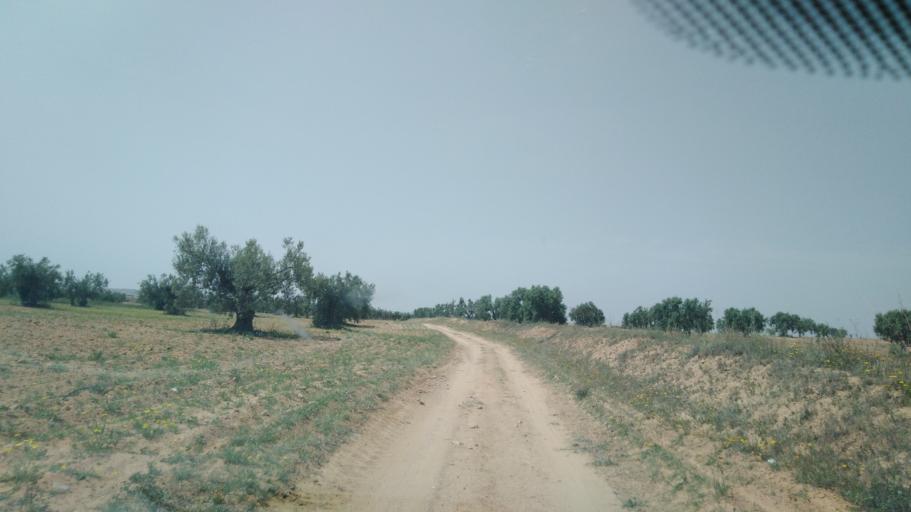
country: TN
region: Safaqis
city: Sfax
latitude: 34.7649
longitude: 10.5814
